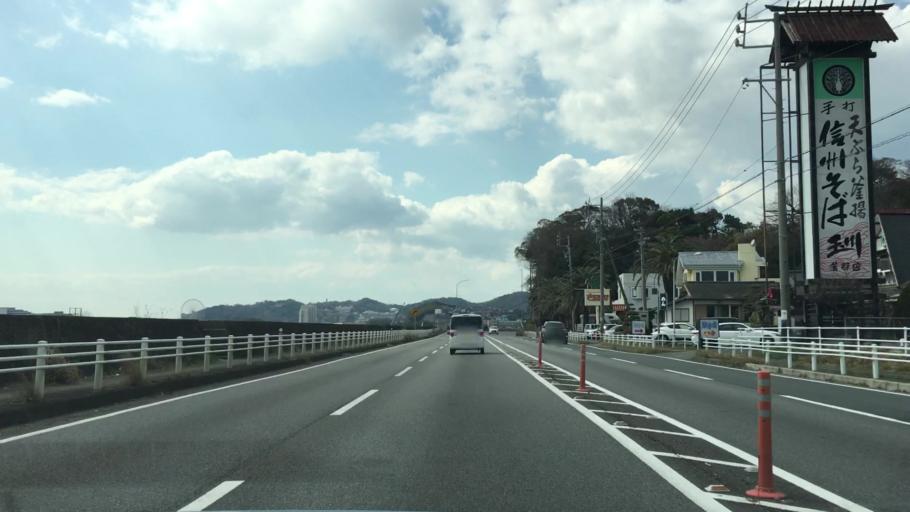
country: JP
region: Aichi
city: Kozakai-cho
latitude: 34.8113
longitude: 137.2977
